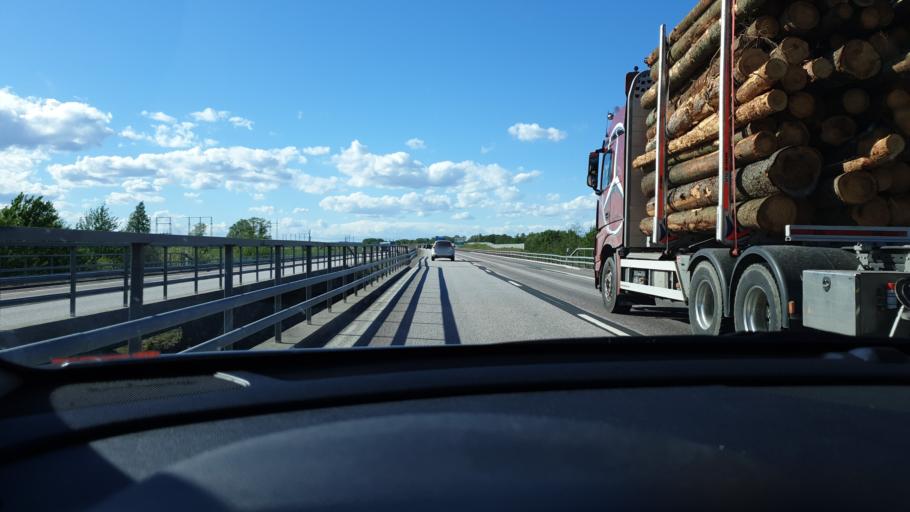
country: SE
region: Uppsala
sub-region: Tierps Kommun
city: Tierp
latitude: 60.3252
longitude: 17.5108
